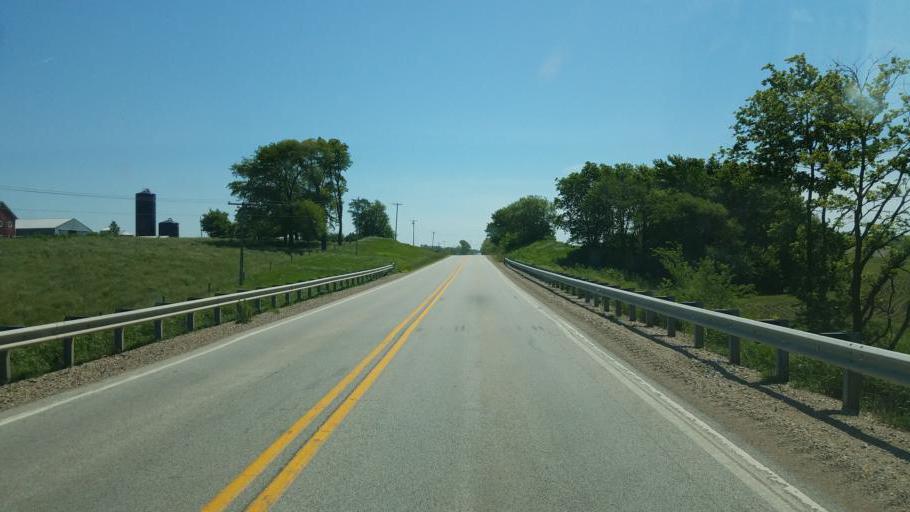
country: US
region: Illinois
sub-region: McLean County
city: Heyworth
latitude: 40.3122
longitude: -89.0293
